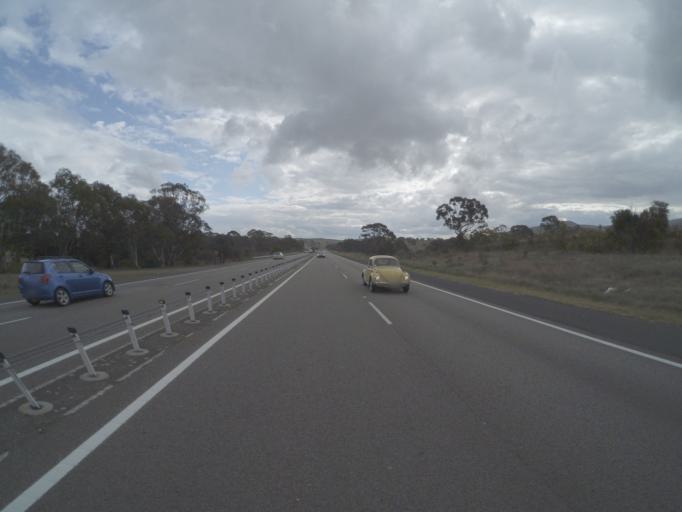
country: AU
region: New South Wales
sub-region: Goulburn Mulwaree
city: Goulburn
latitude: -34.7316
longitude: 149.8153
